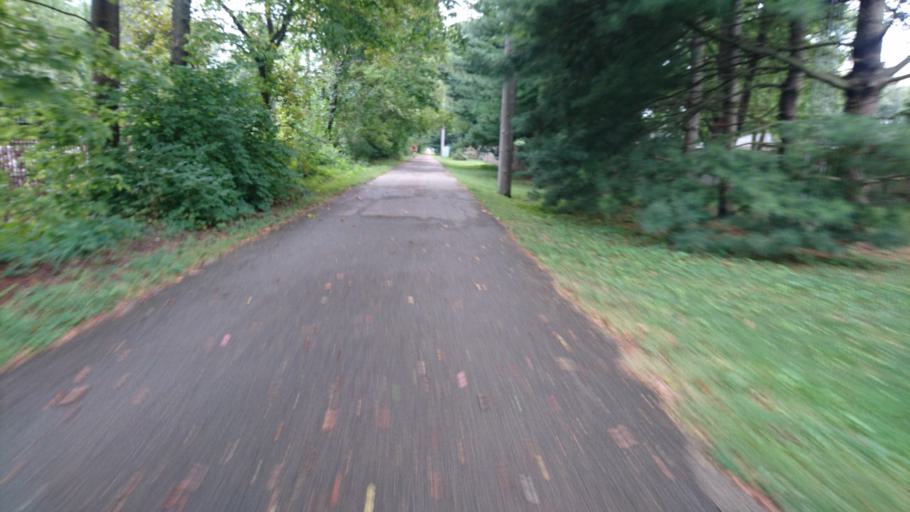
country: US
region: Illinois
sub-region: Sangamon County
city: Chatham
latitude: 39.6823
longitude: -89.6998
